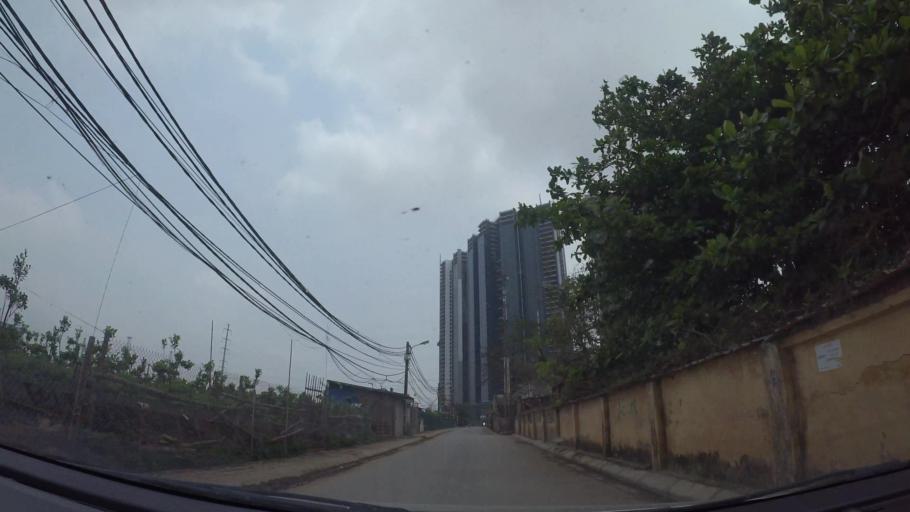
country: VN
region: Ha Noi
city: Tay Ho
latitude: 21.0880
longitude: 105.7919
